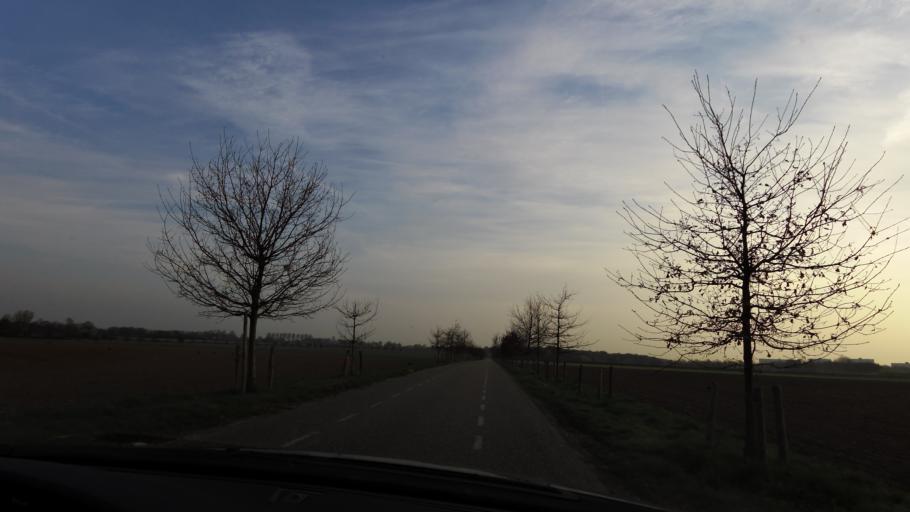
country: NL
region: Limburg
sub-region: Gemeente Schinnen
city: Amstenrade
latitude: 50.9423
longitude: 5.9320
